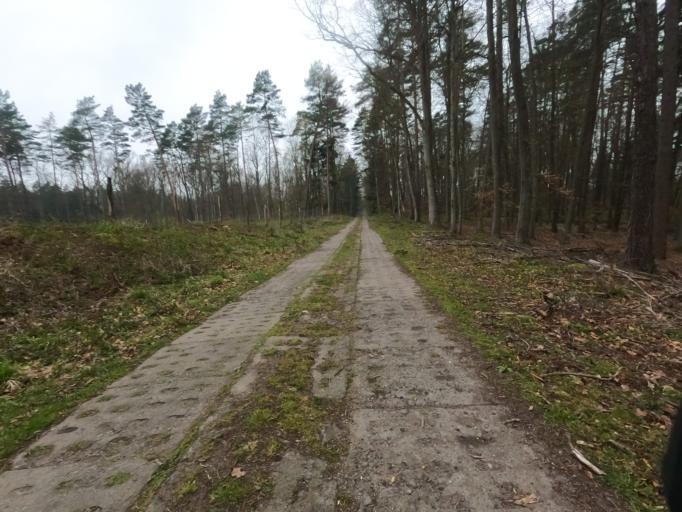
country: PL
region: West Pomeranian Voivodeship
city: Trzcinsko Zdroj
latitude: 52.9278
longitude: 14.6965
